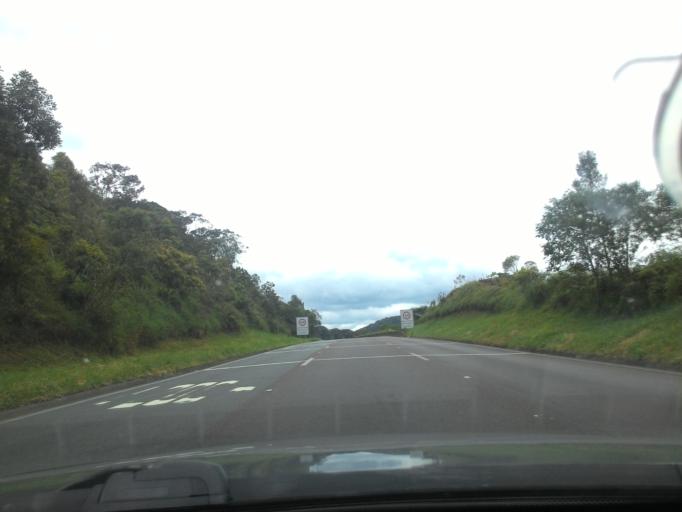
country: BR
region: Sao Paulo
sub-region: Cajati
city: Cajati
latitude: -24.9508
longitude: -48.4246
